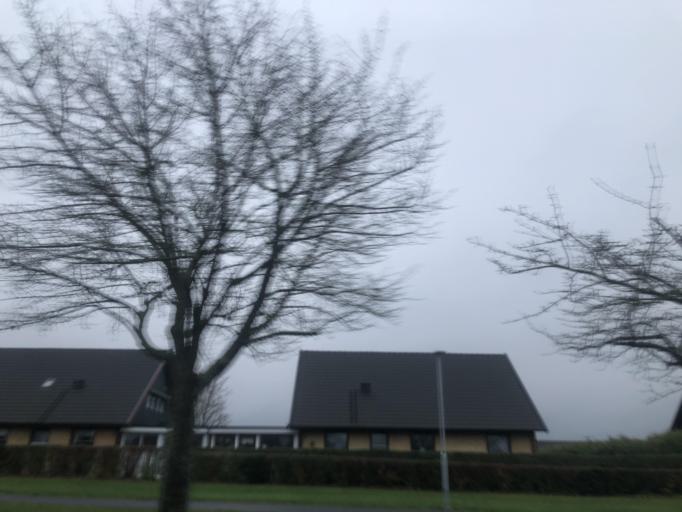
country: SE
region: Skane
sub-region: Trelleborgs Kommun
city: Trelleborg
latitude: 55.3888
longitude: 13.1629
